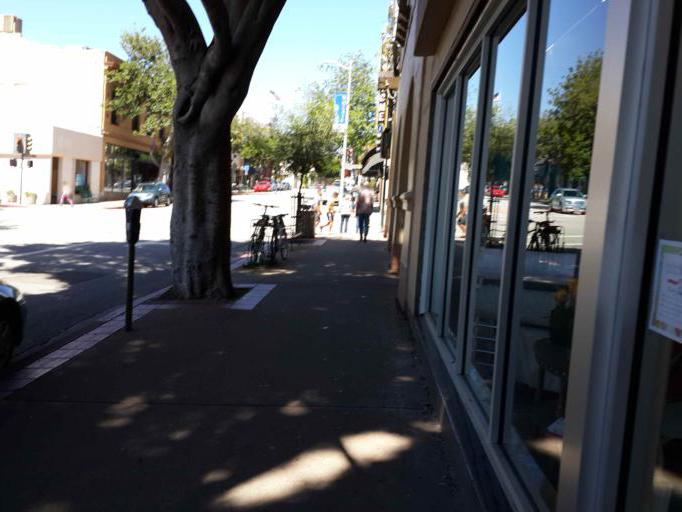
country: US
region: California
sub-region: San Luis Obispo County
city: San Luis Obispo
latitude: 35.2809
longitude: -120.6626
